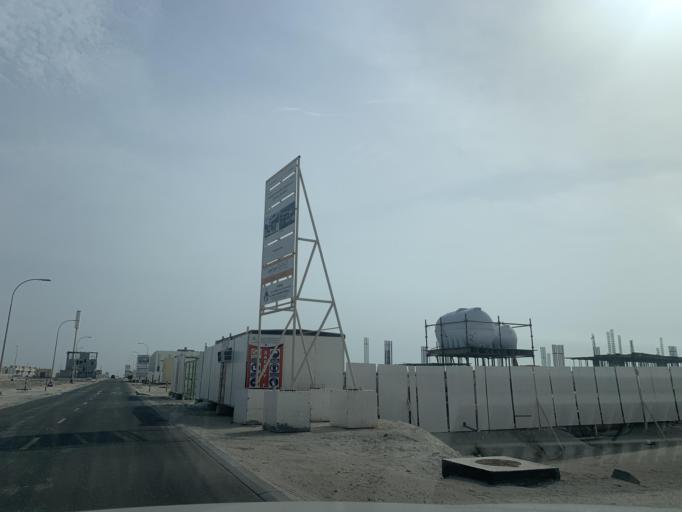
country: BH
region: Muharraq
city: Al Muharraq
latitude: 26.3206
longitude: 50.6227
